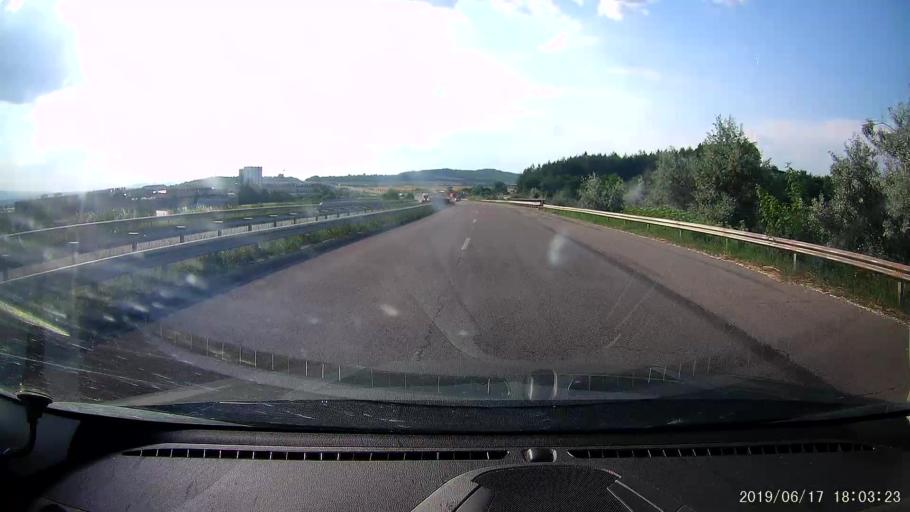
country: BG
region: Khaskovo
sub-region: Obshtina Svilengrad
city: Svilengrad
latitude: 41.7769
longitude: 26.2199
